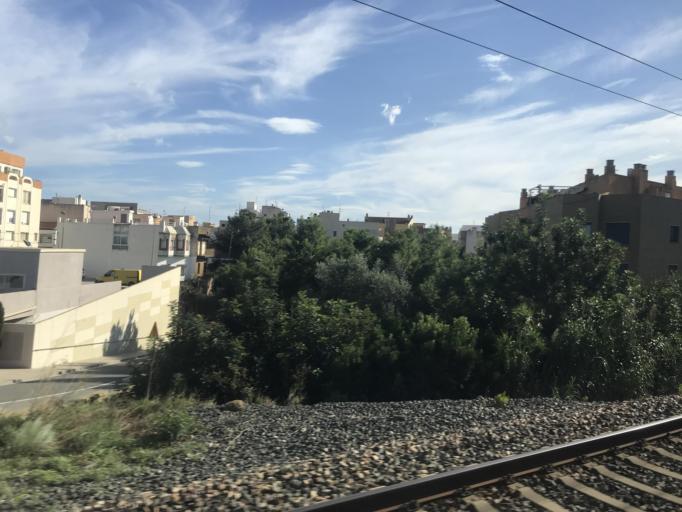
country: ES
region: Catalonia
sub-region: Provincia de Tarragona
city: L'Ampolla
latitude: 40.8143
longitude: 0.7123
